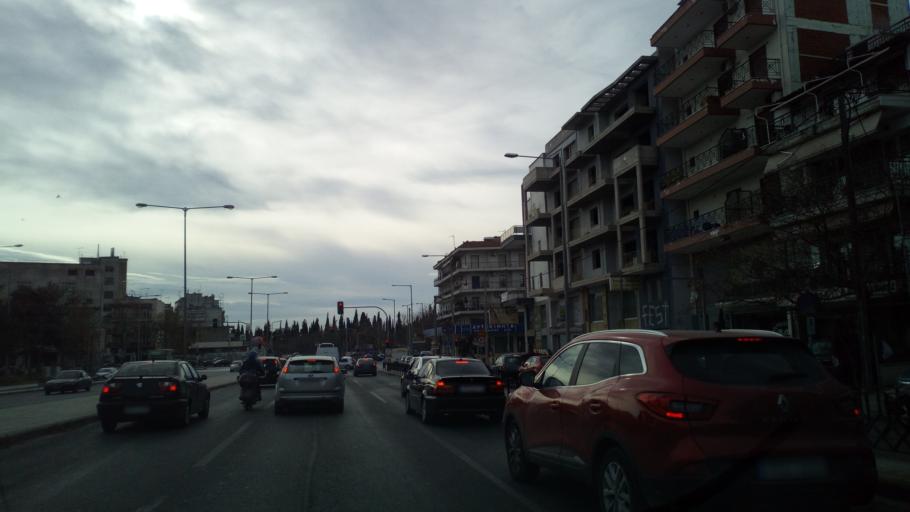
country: GR
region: Central Macedonia
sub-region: Nomos Thessalonikis
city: Ampelokipoi
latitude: 40.6581
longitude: 22.9347
